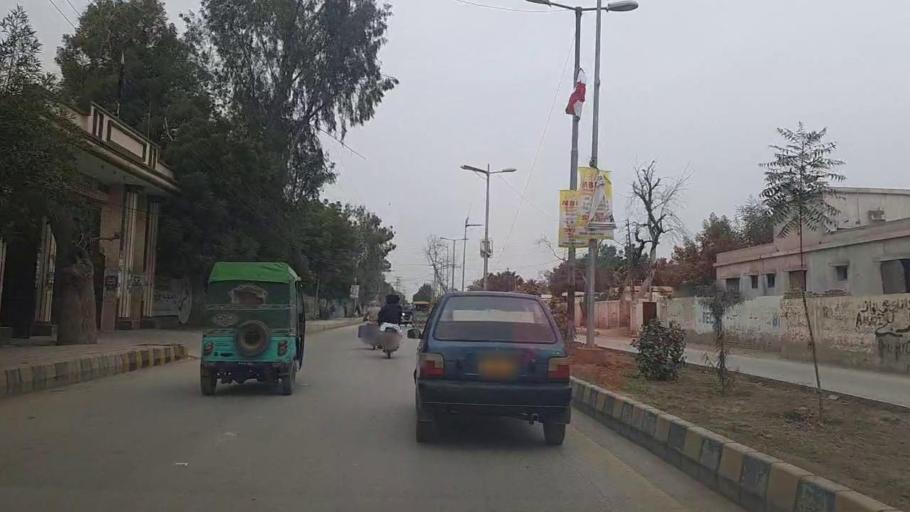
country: PK
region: Sindh
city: Nawabshah
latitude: 26.2454
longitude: 68.4017
